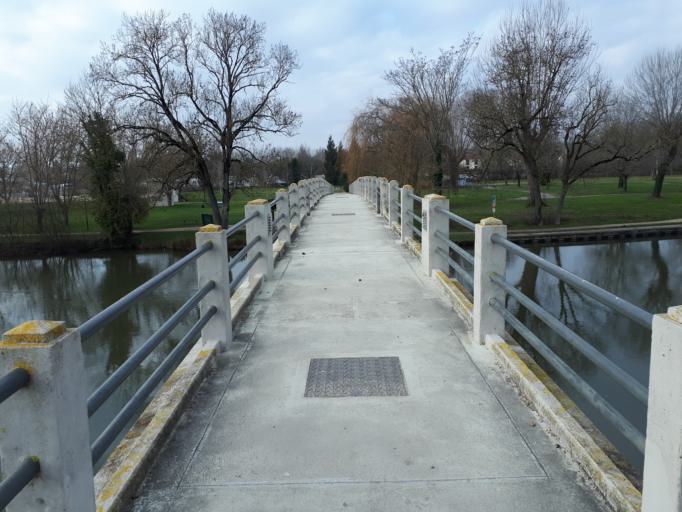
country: FR
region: Poitou-Charentes
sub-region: Departement de la Charente
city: Angouleme
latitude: 45.6590
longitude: 0.1599
